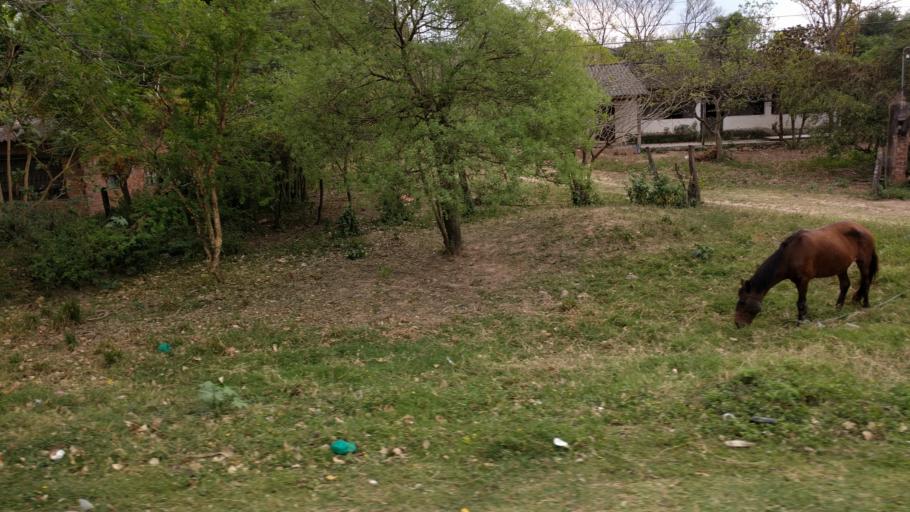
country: BO
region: Santa Cruz
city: Jorochito
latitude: -18.1199
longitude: -63.4625
